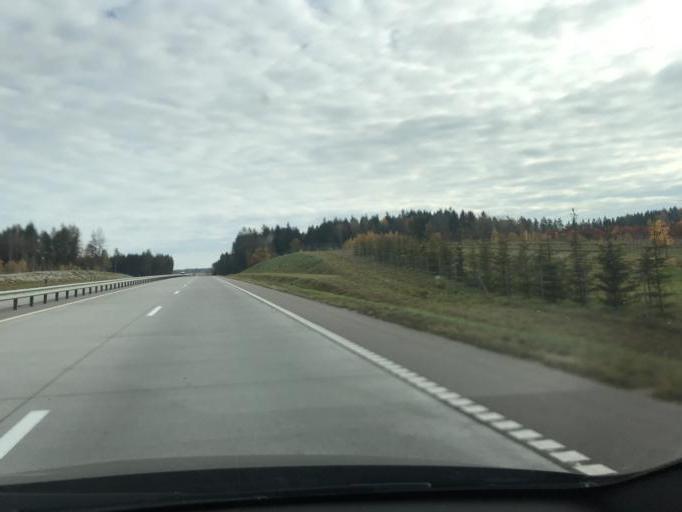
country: BY
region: Minsk
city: Syomkava
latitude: 54.0635
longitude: 27.3665
